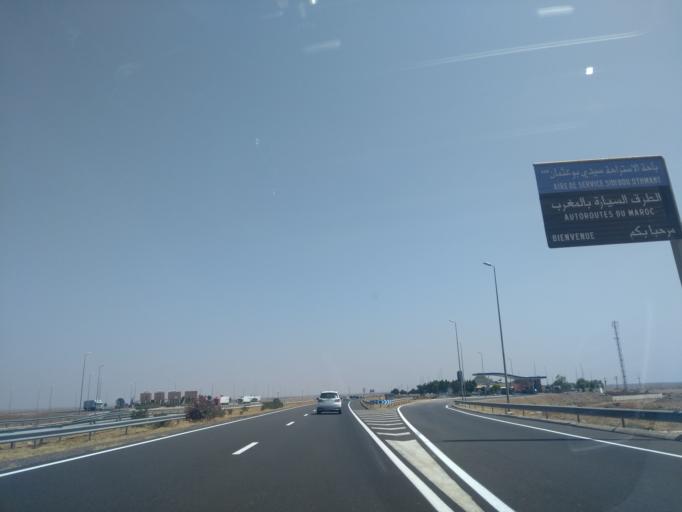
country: MA
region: Marrakech-Tensift-Al Haouz
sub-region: Kelaa-Des-Sraghna
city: Sidi Bou Othmane
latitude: 31.9163
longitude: -8.0252
